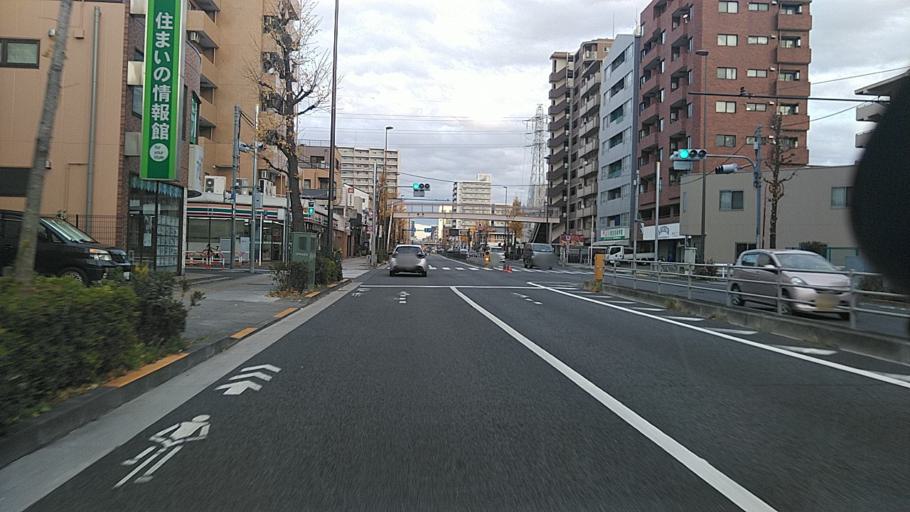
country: JP
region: Saitama
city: Soka
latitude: 35.7714
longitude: 139.8034
